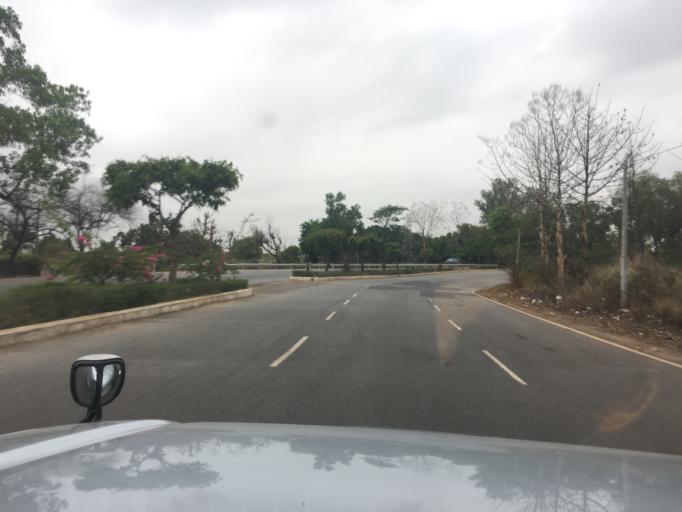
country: MM
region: Bago
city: Thanatpin
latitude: 17.2110
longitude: 96.4168
